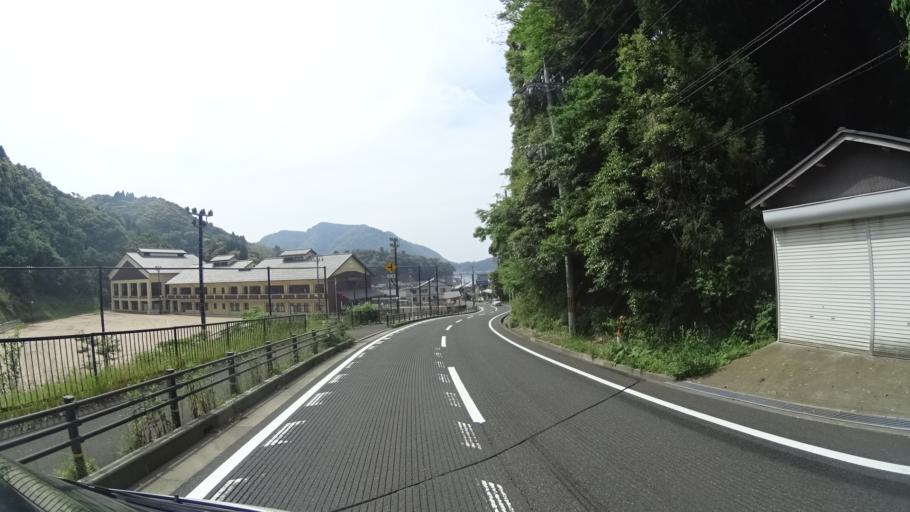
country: JP
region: Kyoto
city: Miyazu
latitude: 35.6786
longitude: 135.2864
